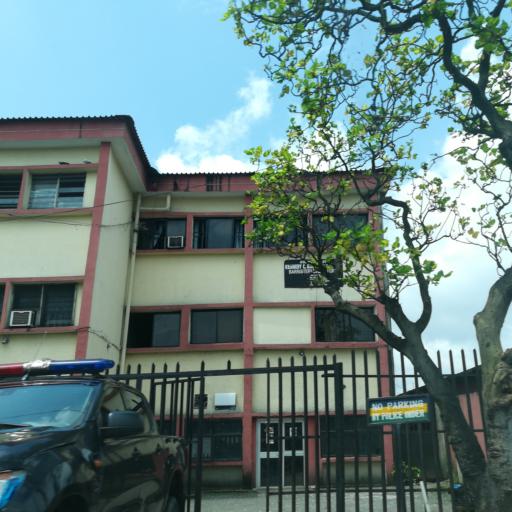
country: NG
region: Rivers
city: Port Harcourt
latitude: 4.8006
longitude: 7.0036
